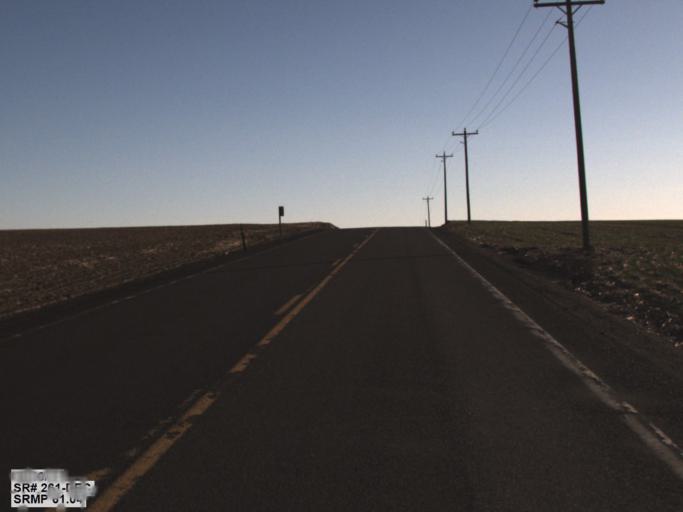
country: US
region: Washington
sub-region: Adams County
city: Ritzville
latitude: 47.0911
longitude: -118.3654
